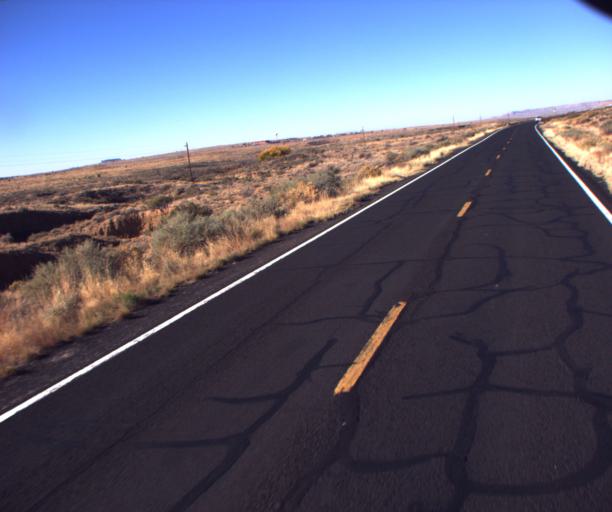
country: US
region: Arizona
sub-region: Navajo County
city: First Mesa
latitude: 35.8299
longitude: -110.2791
